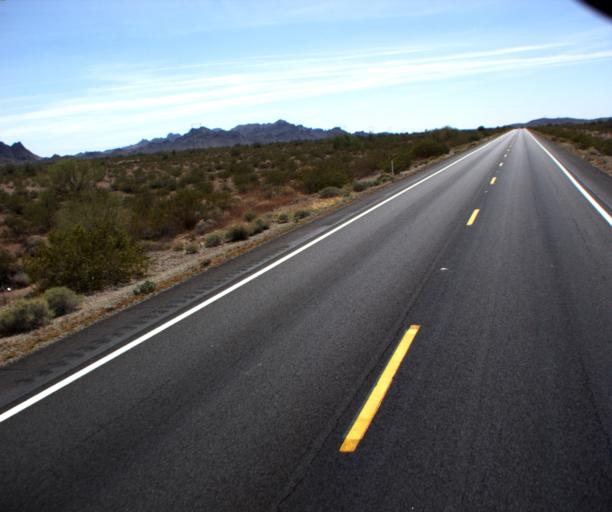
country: US
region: Arizona
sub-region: La Paz County
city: Quartzsite
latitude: 33.2912
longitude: -114.2253
